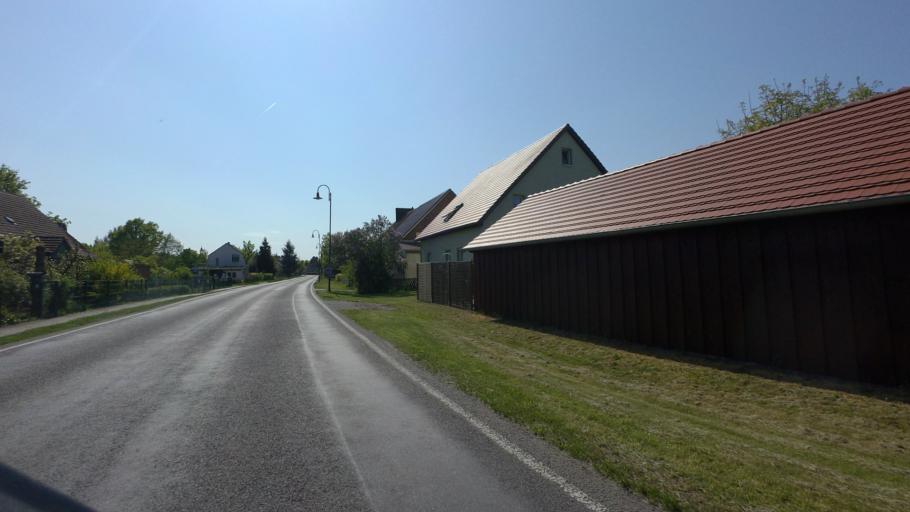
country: DE
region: Brandenburg
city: Tauche
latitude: 52.0652
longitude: 14.1467
